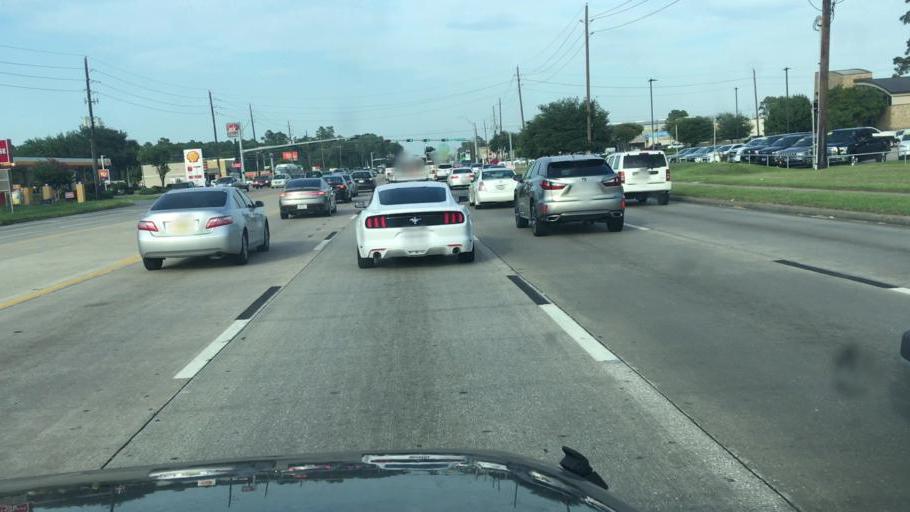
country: US
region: Texas
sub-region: Harris County
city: Spring
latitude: 30.0232
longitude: -95.4223
